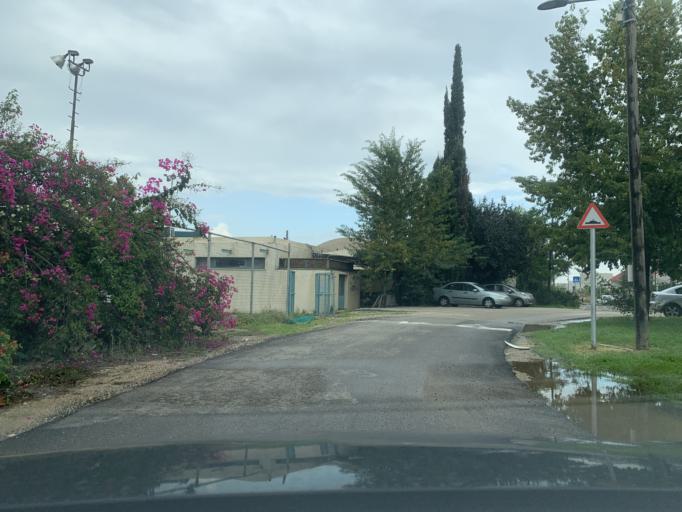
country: PS
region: West Bank
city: Qalqilyah
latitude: 32.2117
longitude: 34.9767
